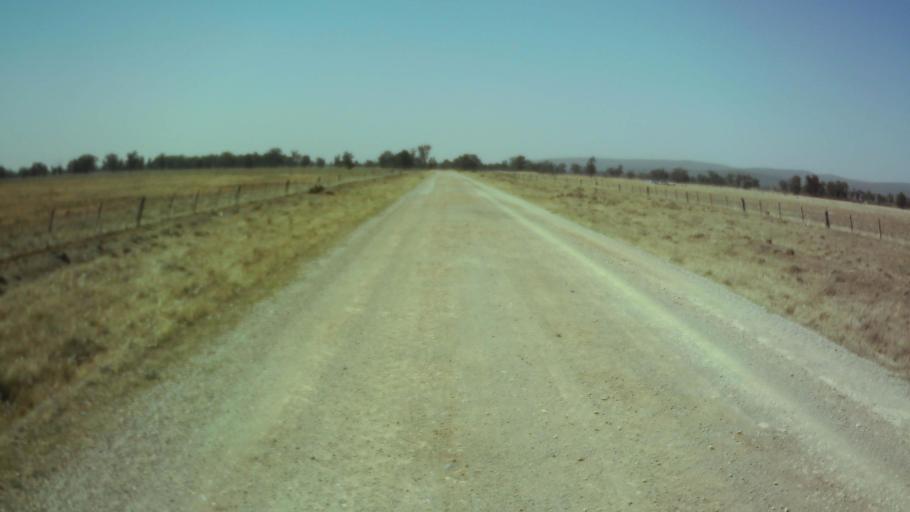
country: AU
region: New South Wales
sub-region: Weddin
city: Grenfell
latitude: -34.0306
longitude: 147.9125
